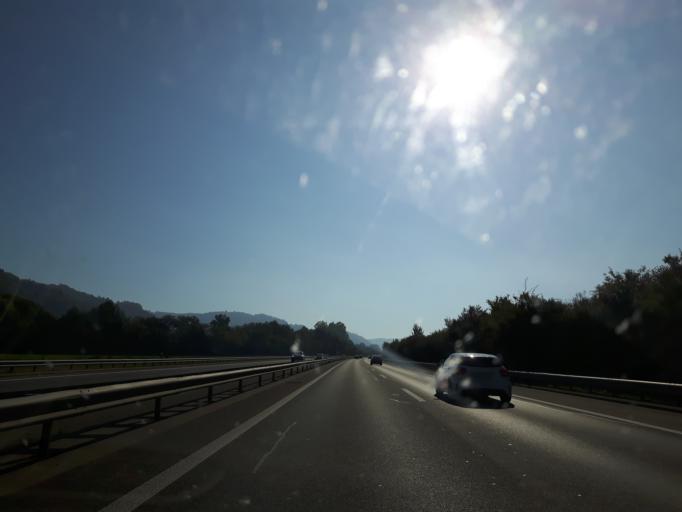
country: CH
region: Lucerne
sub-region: Willisau District
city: Reiden
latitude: 47.2367
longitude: 7.9636
